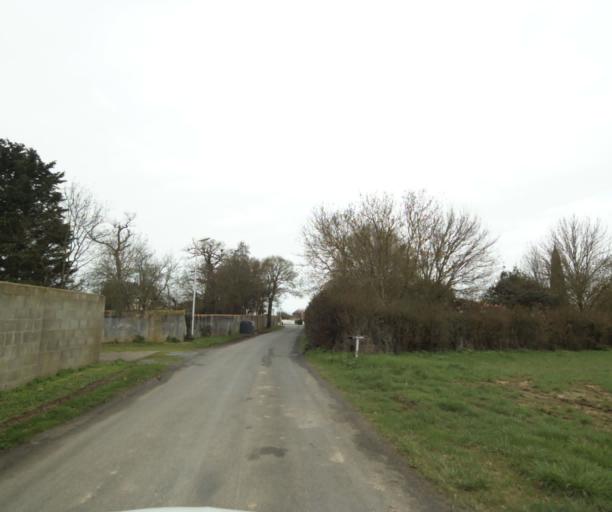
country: FR
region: Poitou-Charentes
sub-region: Departement de la Charente-Maritime
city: Nieul-sur-Mer
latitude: 46.1934
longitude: -1.1709
